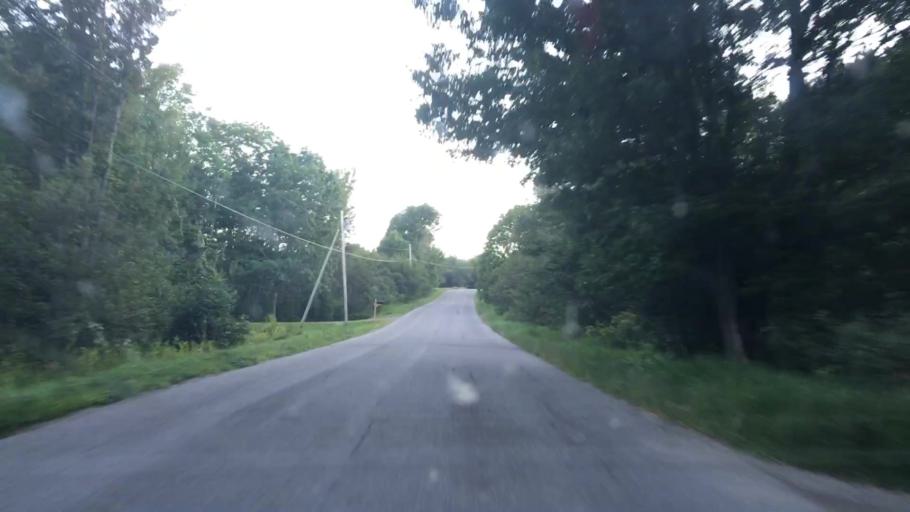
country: US
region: Maine
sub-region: Waldo County
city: Frankfort
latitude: 44.6590
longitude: -68.9348
